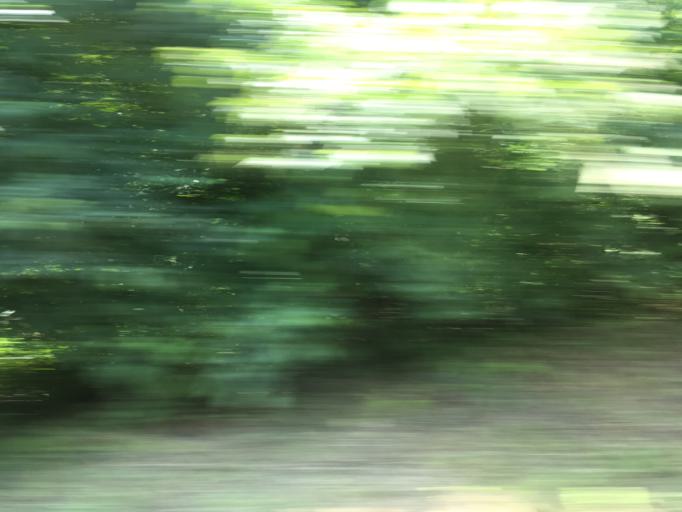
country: SI
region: Metlika
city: Metlika
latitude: 45.5964
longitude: 15.3413
